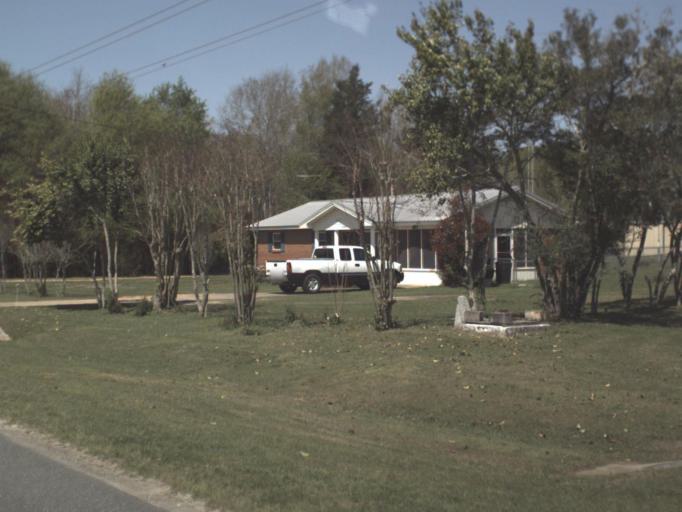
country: US
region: Florida
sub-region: Jackson County
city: Graceville
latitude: 30.9637
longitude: -85.5660
